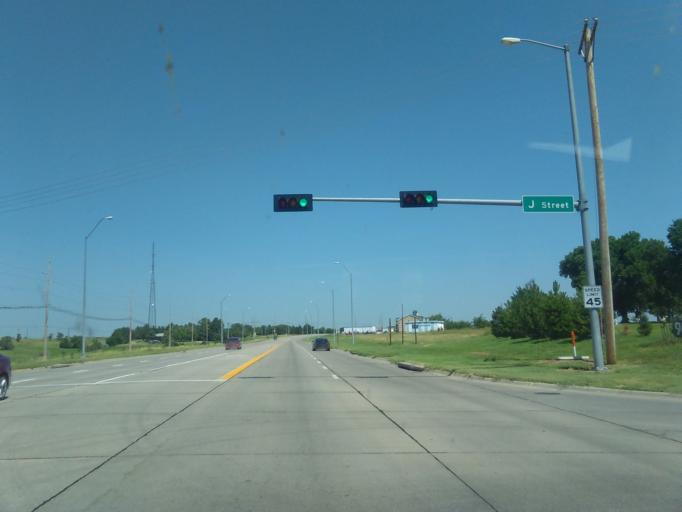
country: US
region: Nebraska
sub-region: Red Willow County
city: McCook
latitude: 40.2071
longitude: -100.6476
